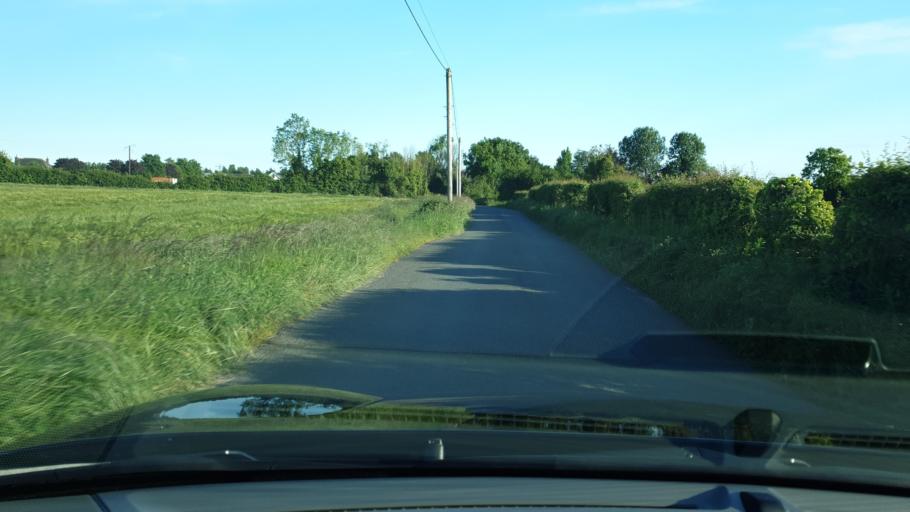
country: IE
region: Leinster
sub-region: Fingal County
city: Swords
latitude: 53.4885
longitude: -6.2272
